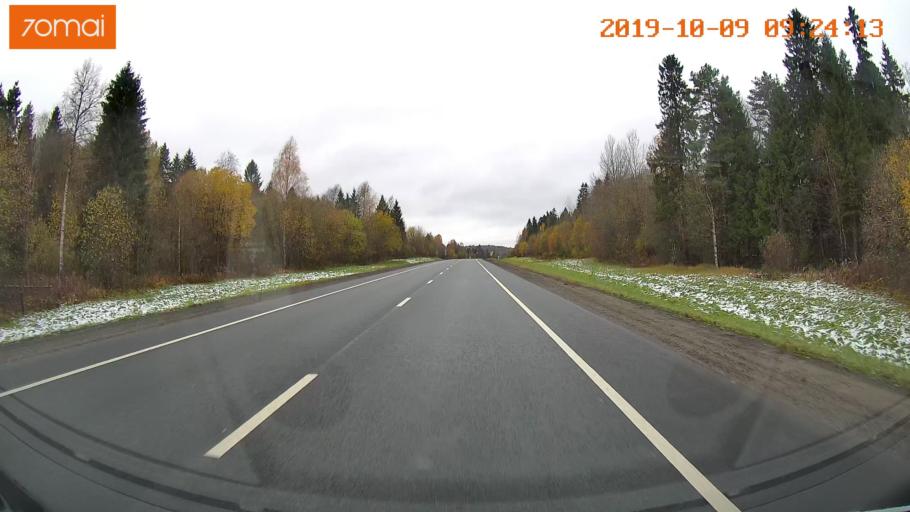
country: RU
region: Vologda
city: Vologda
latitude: 59.0766
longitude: 40.0196
